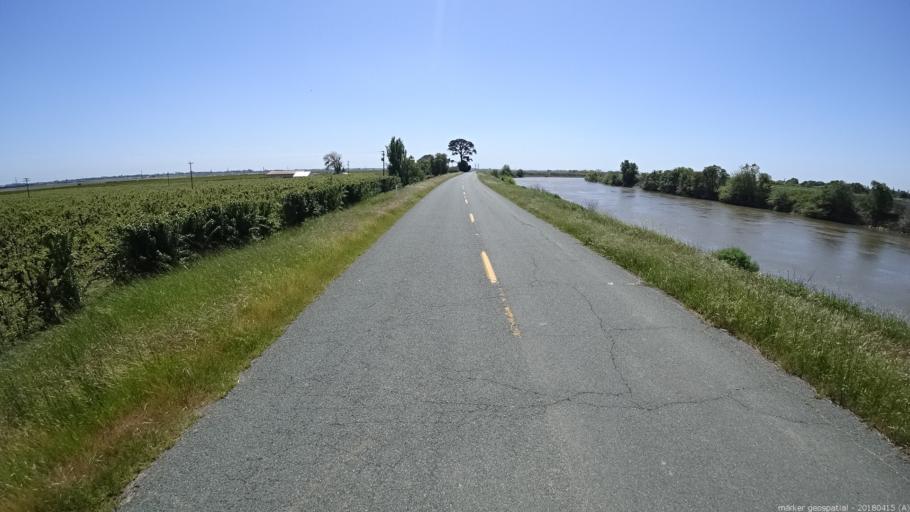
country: US
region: California
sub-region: Sacramento County
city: Walnut Grove
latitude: 38.2663
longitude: -121.5871
